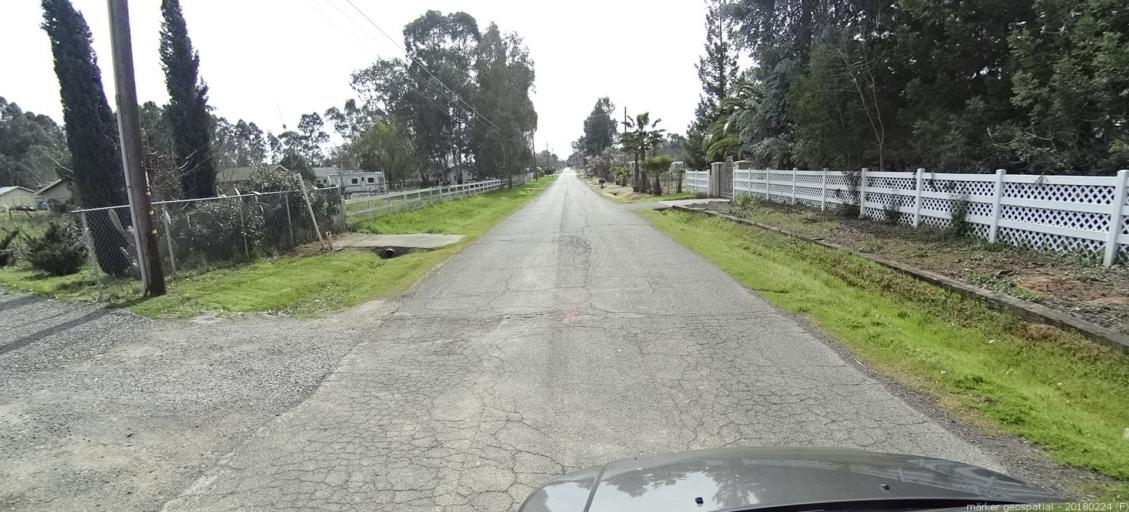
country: US
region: California
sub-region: Sacramento County
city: Elverta
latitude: 38.7119
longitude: -121.4542
